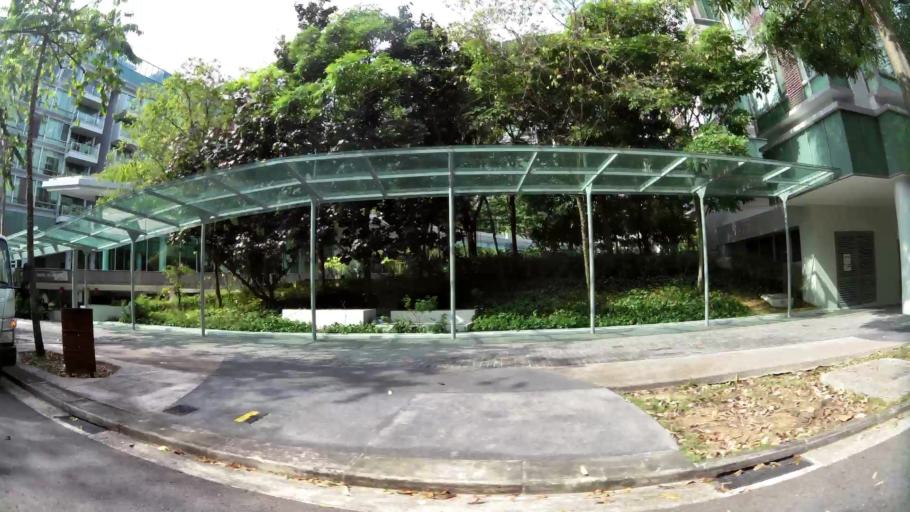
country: SG
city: Singapore
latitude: 1.3028
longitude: 103.7899
